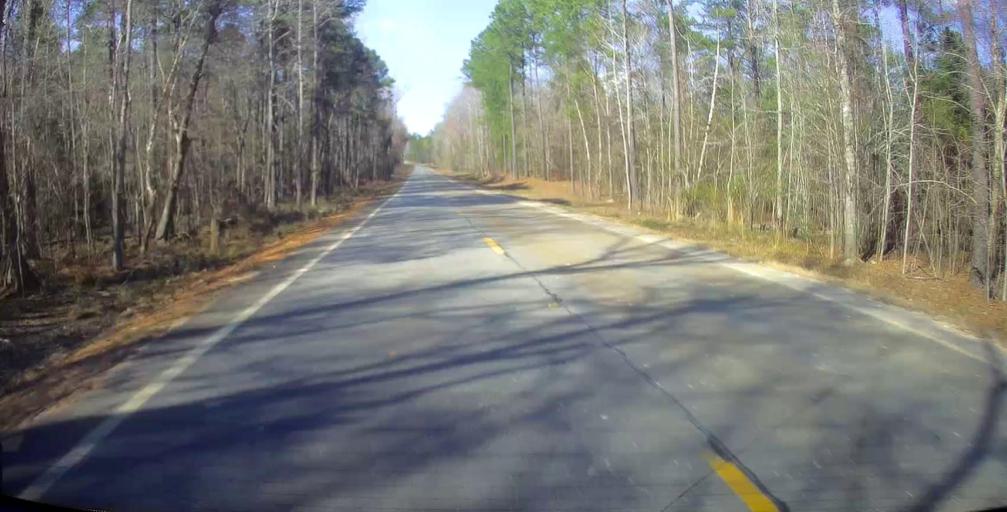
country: US
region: Georgia
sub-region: Wilkinson County
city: Gordon
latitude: 32.8168
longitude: -83.3244
